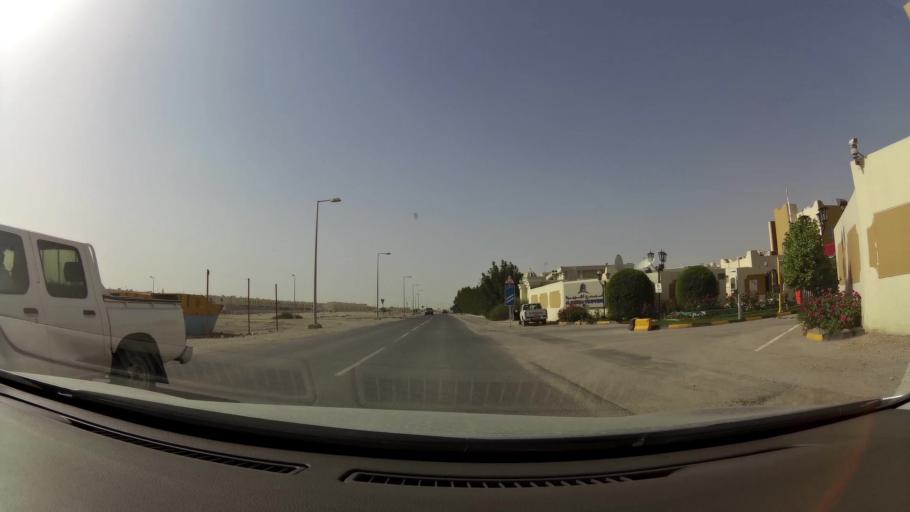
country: QA
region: Baladiyat ar Rayyan
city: Ar Rayyan
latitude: 25.3438
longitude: 51.4543
